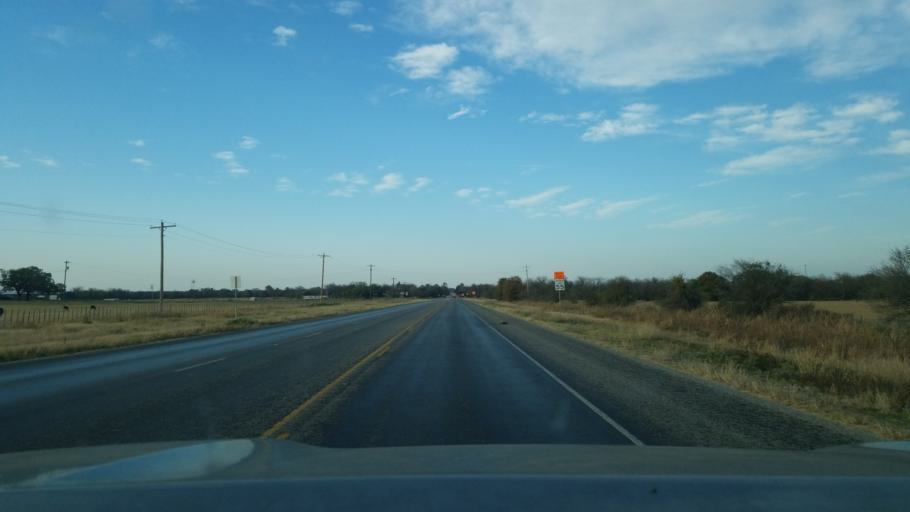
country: US
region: Texas
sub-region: Brown County
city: Lake Brownwood
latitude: 32.0797
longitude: -98.9640
